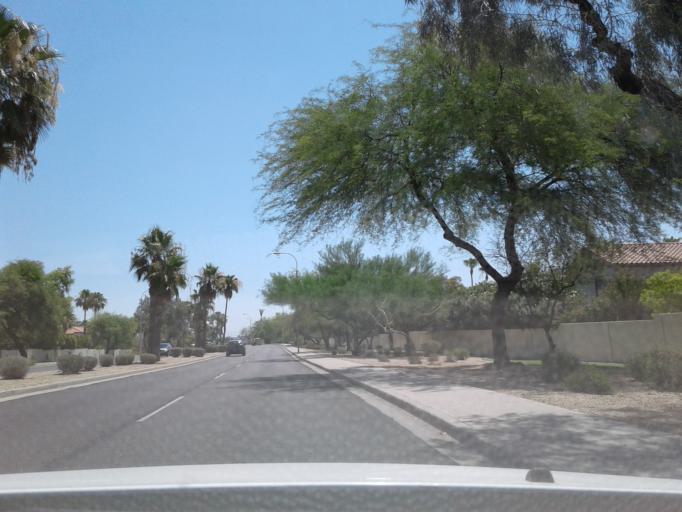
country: US
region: Arizona
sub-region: Maricopa County
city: Guadalupe
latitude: 33.3638
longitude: -111.9735
